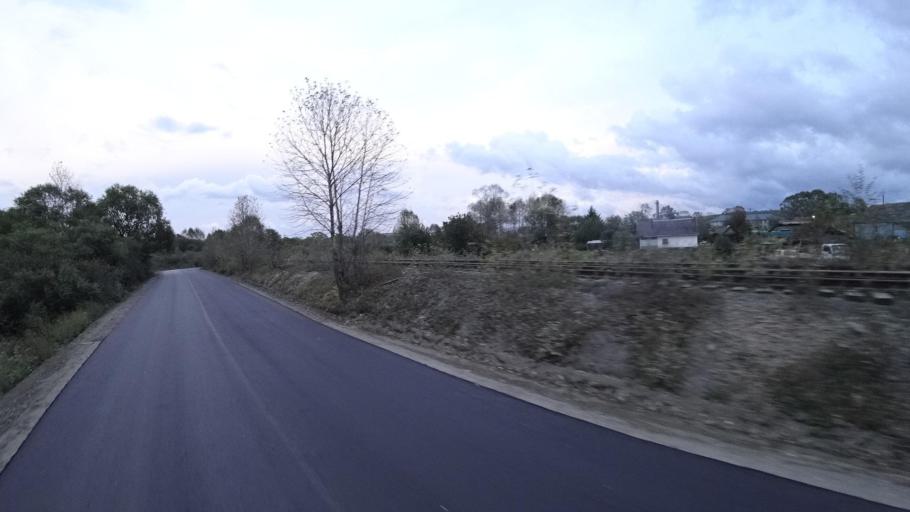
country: RU
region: Jewish Autonomous Oblast
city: Izvestkovyy
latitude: 48.9897
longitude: 131.5505
